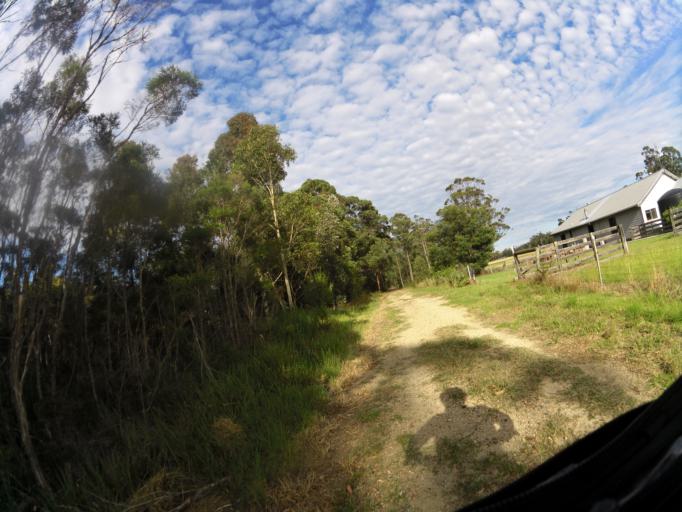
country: AU
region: Victoria
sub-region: East Gippsland
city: Lakes Entrance
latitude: -37.7458
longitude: 148.4074
